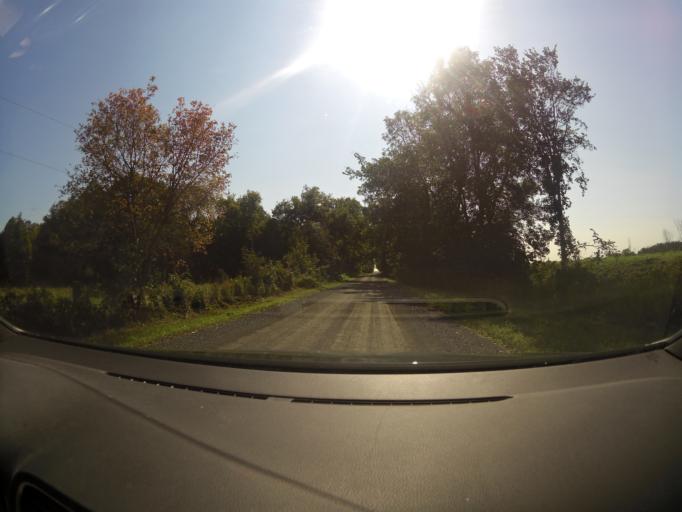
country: CA
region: Ontario
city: Arnprior
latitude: 45.3531
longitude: -76.2581
